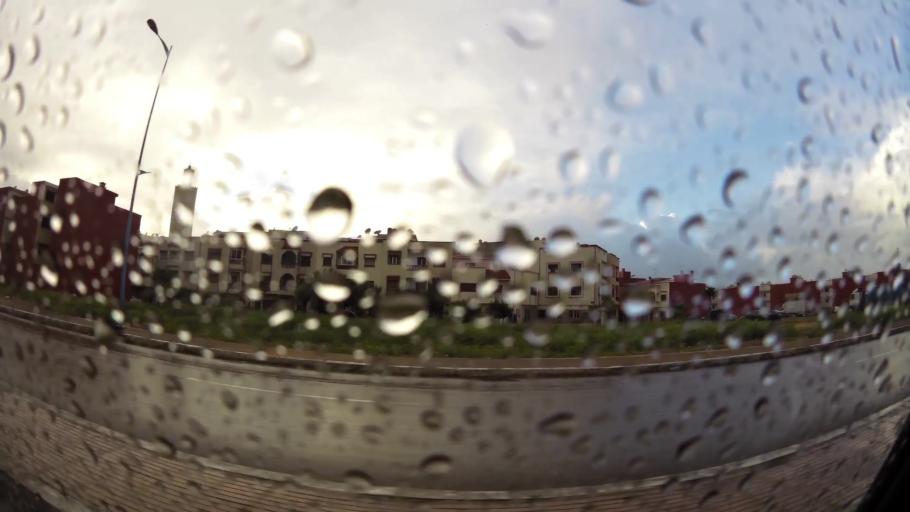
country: MA
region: Doukkala-Abda
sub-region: El-Jadida
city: El Jadida
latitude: 33.2371
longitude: -8.5211
